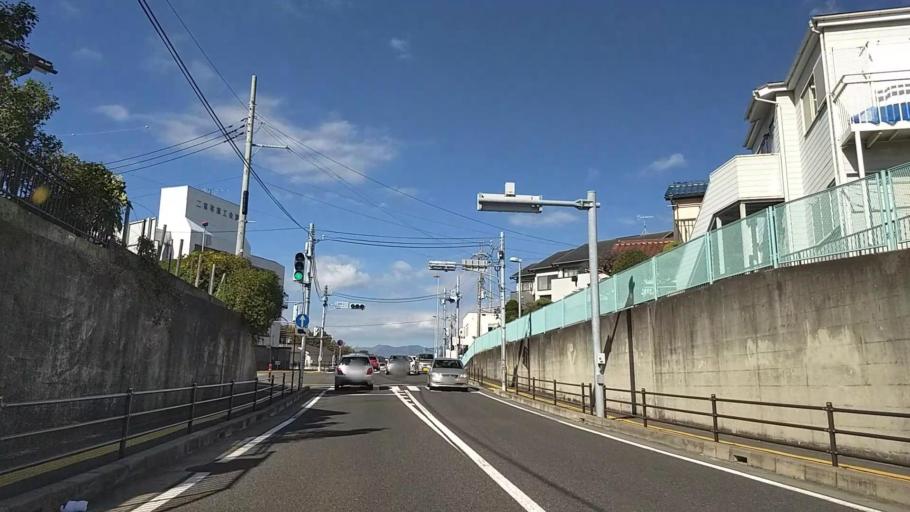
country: JP
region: Kanagawa
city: Ninomiya
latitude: 35.3004
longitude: 139.2599
